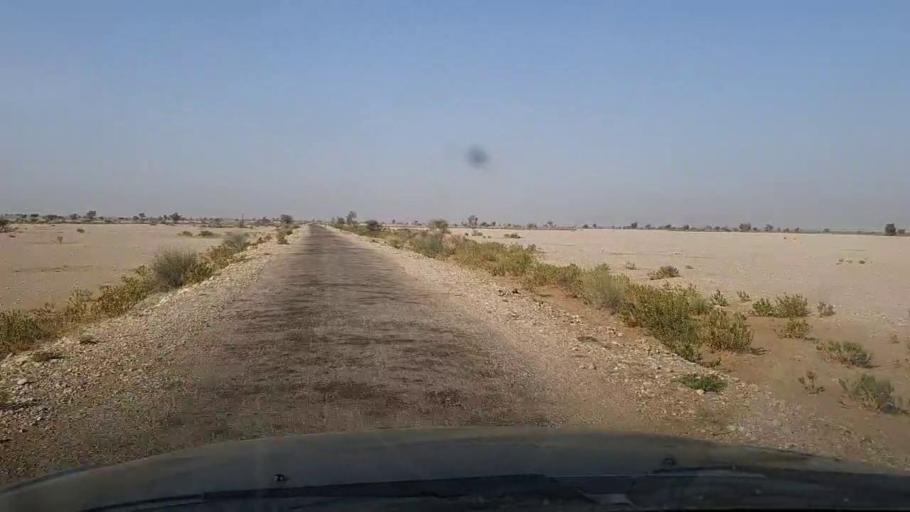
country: PK
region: Sindh
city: Sann
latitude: 25.9845
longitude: 68.0631
